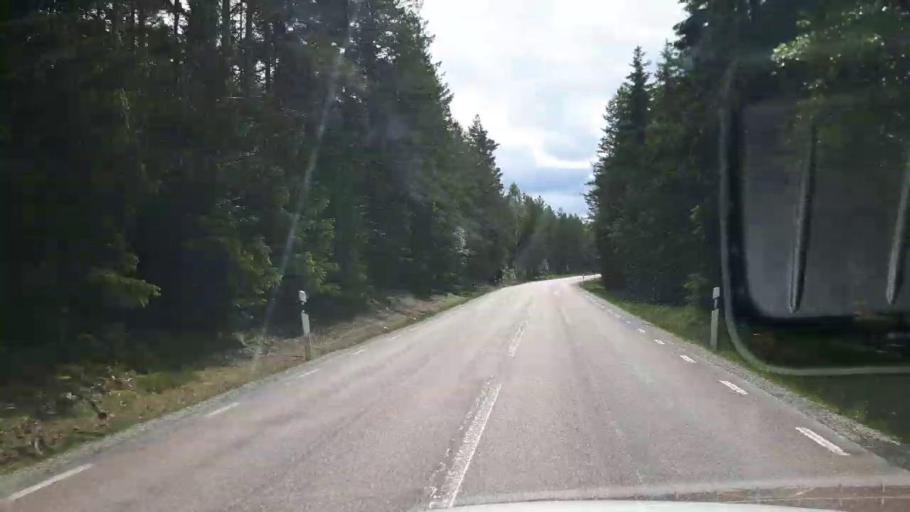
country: SE
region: Vaestmanland
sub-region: Fagersta Kommun
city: Fagersta
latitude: 59.9058
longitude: 15.8227
